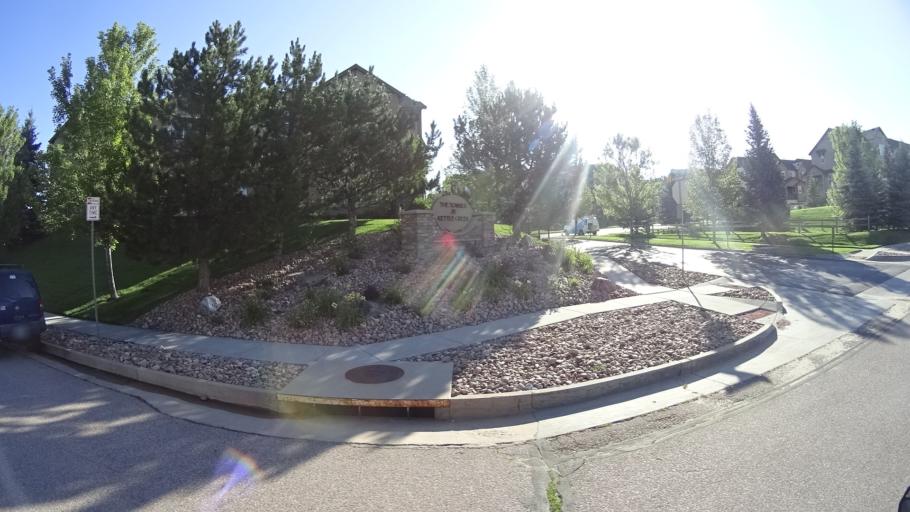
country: US
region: Colorado
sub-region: El Paso County
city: Black Forest
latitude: 38.9856
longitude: -104.7697
